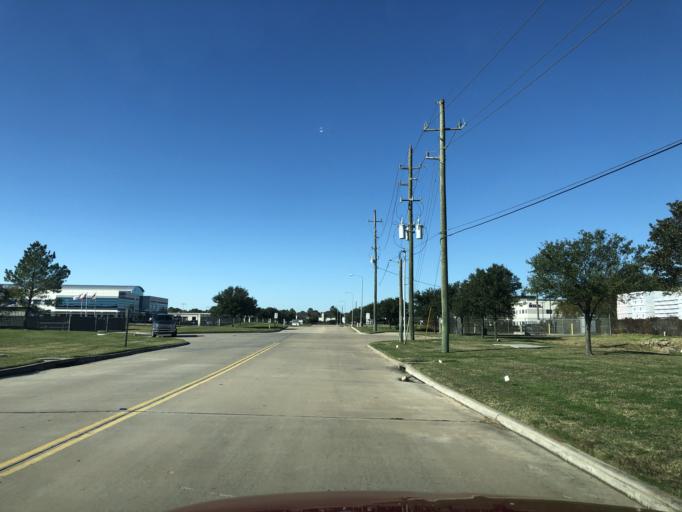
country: US
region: Texas
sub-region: Harris County
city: Oak Cliff Place
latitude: 29.9362
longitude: -95.6553
